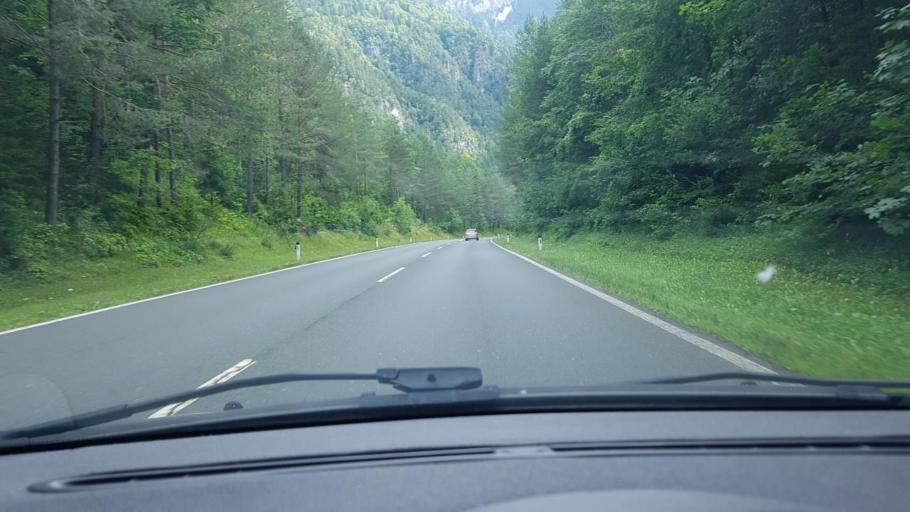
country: AT
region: Carinthia
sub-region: Politischer Bezirk Hermagor
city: Hermagor
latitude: 46.6310
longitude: 13.4334
